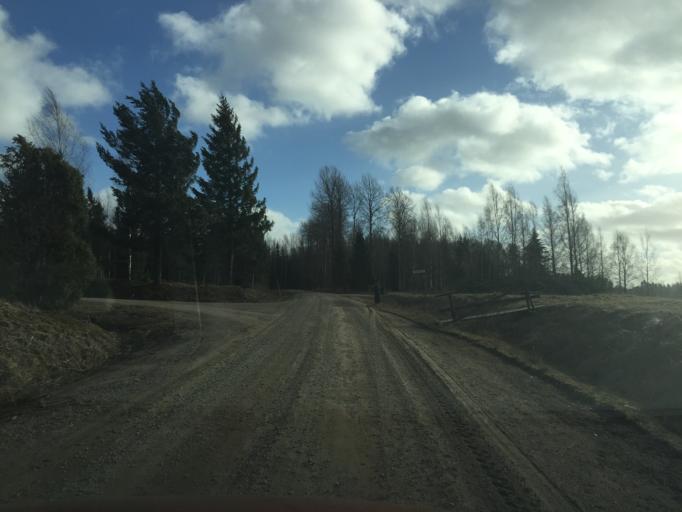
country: SE
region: Soedermanland
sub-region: Vingakers Kommun
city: Vingaker
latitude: 58.9969
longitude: 15.7392
